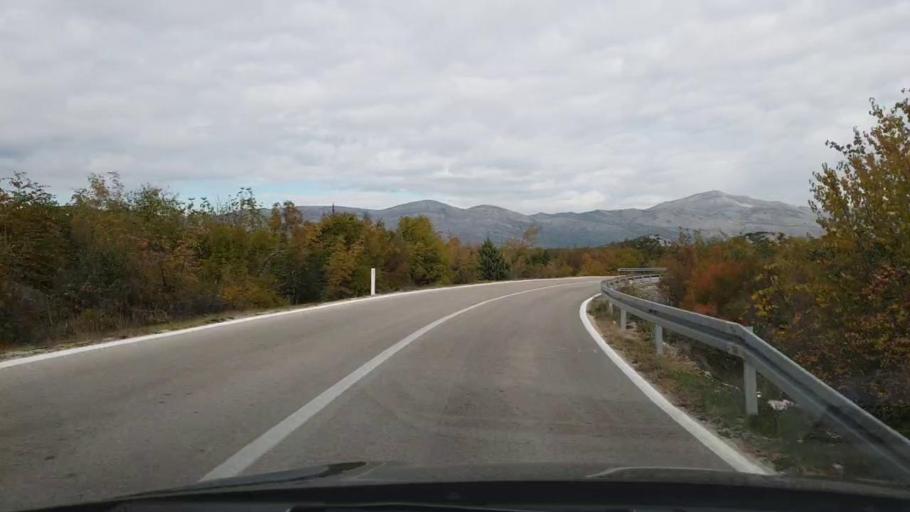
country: HR
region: Dubrovacko-Neretvanska
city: Cibaca
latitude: 42.6771
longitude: 18.2358
